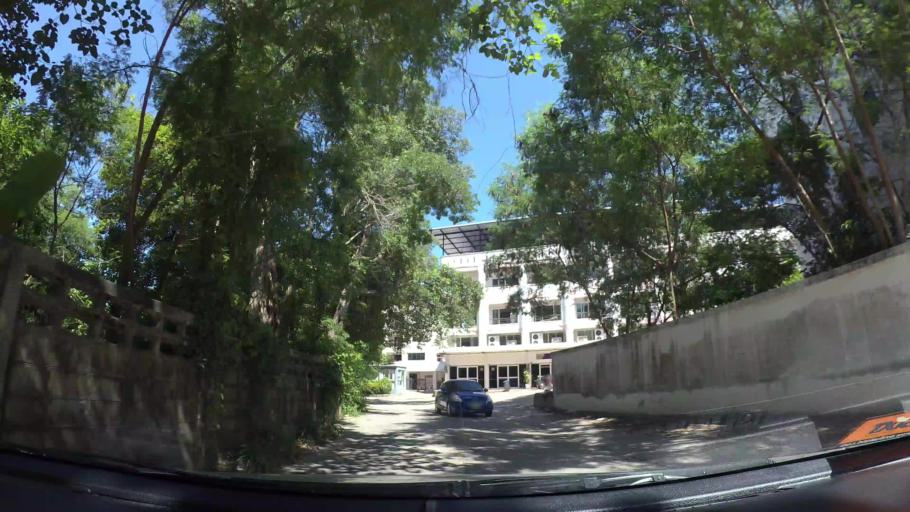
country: TH
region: Chon Buri
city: Si Racha
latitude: 13.1617
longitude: 100.9335
